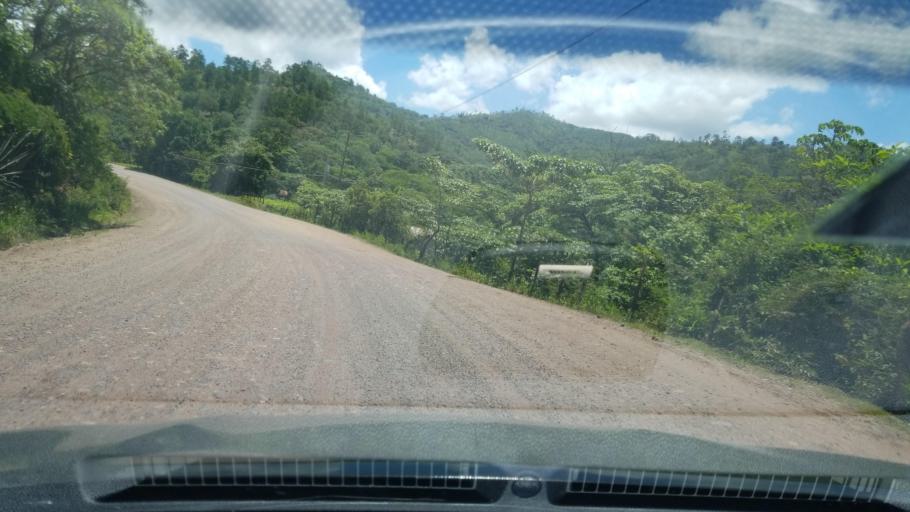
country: HN
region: Francisco Morazan
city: San Juan de Flores
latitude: 14.3372
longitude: -87.0436
